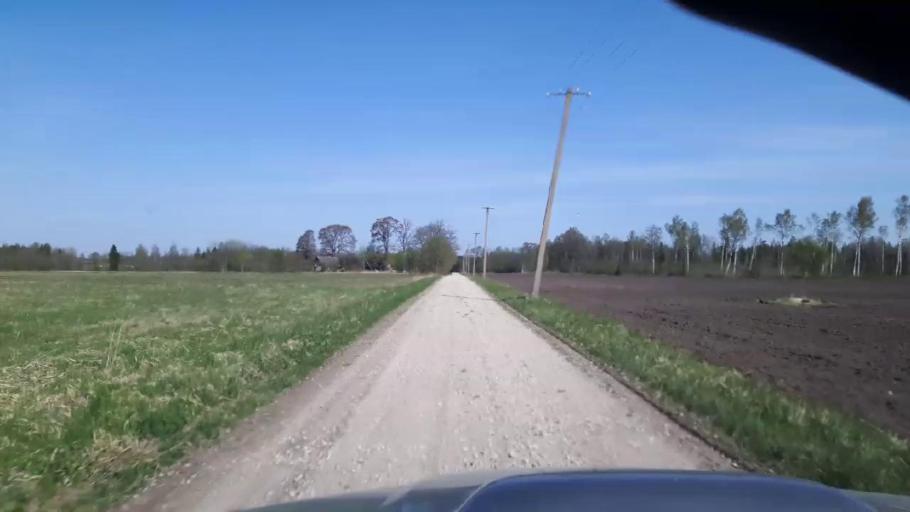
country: EE
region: Paernumaa
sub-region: Tootsi vald
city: Tootsi
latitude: 58.4912
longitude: 24.9312
